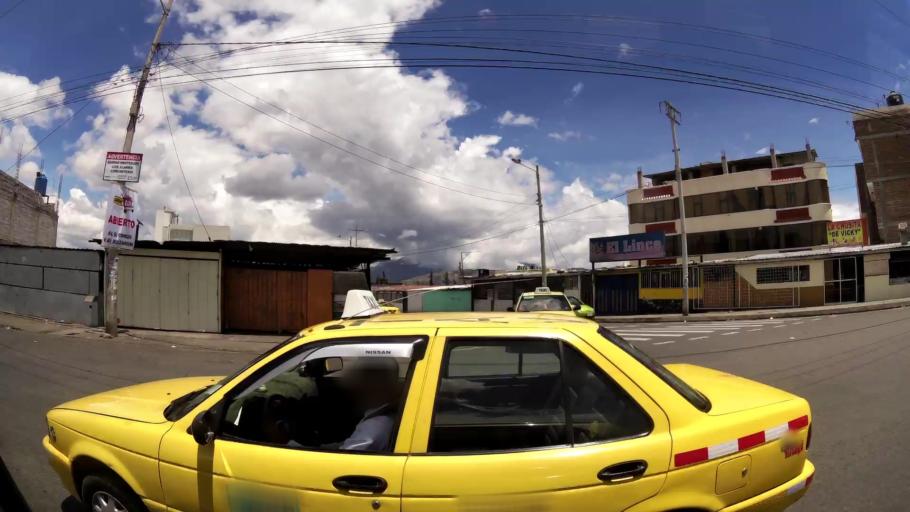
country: EC
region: Tungurahua
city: Ambato
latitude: -1.2708
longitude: -78.6116
